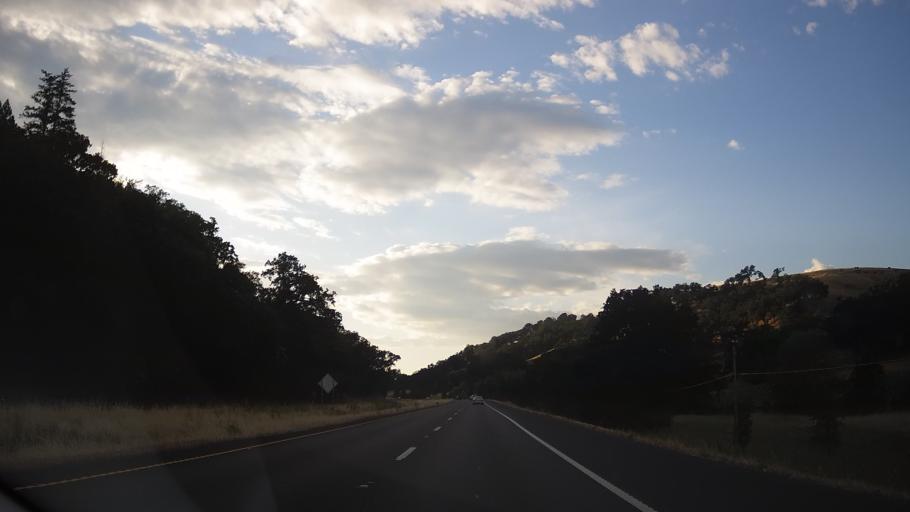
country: US
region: California
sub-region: Mendocino County
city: Talmage
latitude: 39.0599
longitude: -123.1608
